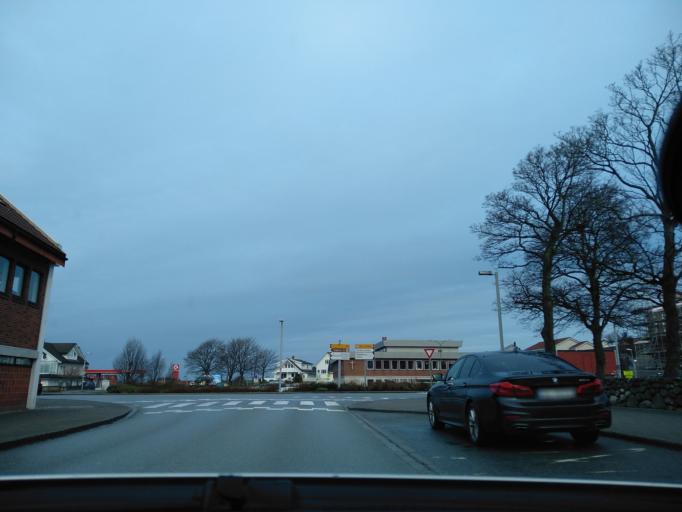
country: NO
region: Rogaland
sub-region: Randaberg
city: Randaberg
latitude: 58.9999
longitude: 5.6187
